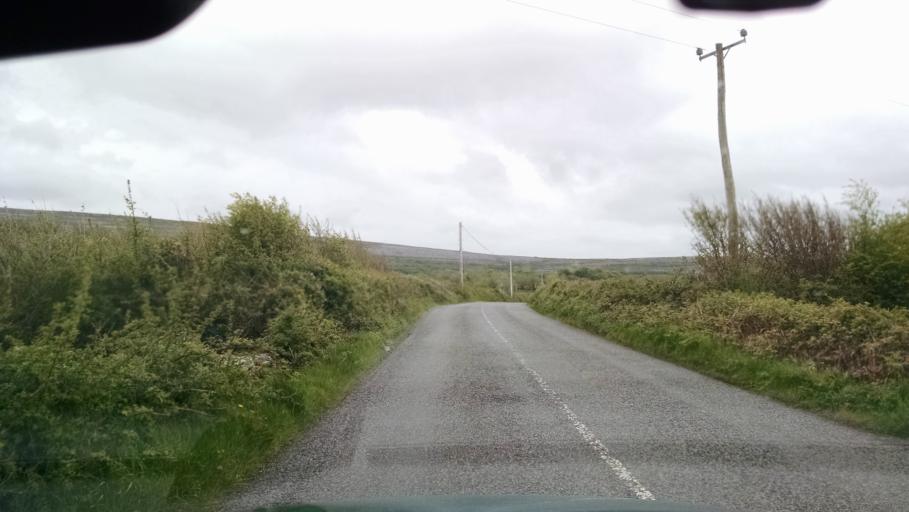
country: IE
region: Connaught
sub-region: County Galway
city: Bearna
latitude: 53.0962
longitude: -9.1592
